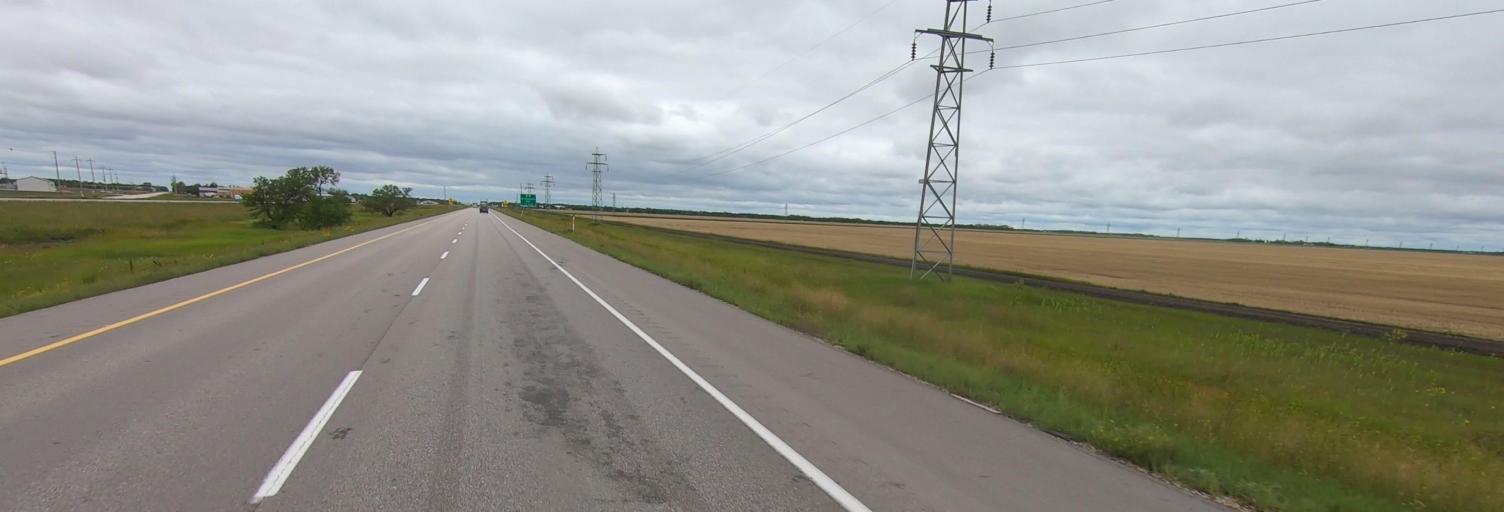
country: CA
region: Manitoba
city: Headingley
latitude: 49.8994
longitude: -97.7310
